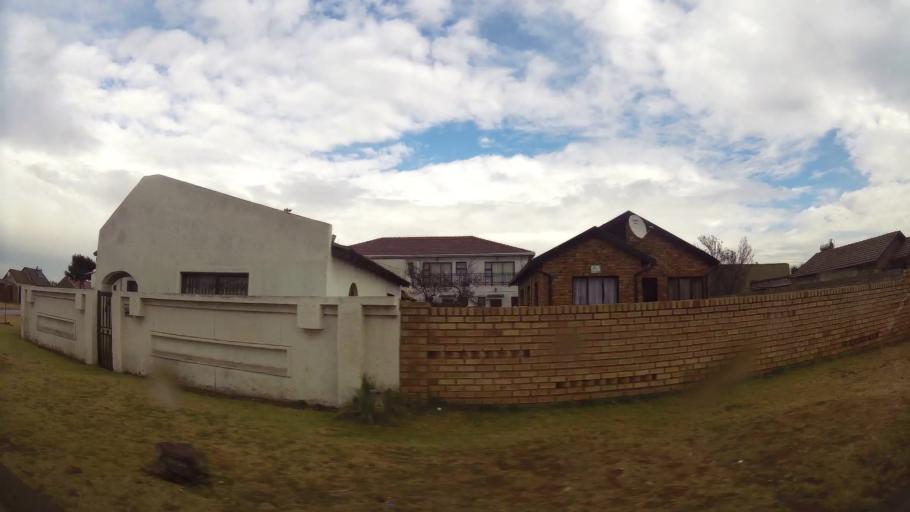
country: ZA
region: Gauteng
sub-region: Ekurhuleni Metropolitan Municipality
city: Germiston
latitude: -26.3275
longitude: 28.1974
